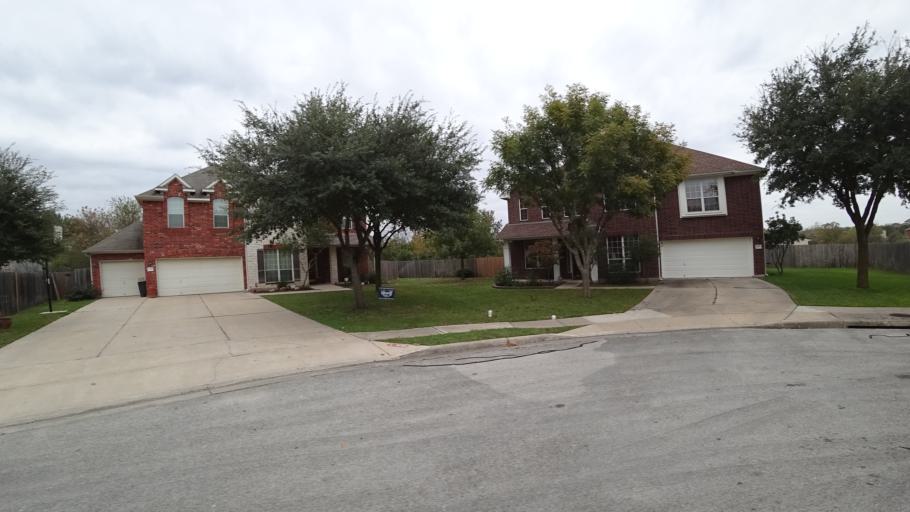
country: US
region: Texas
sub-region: Travis County
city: Pflugerville
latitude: 30.4508
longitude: -97.6242
